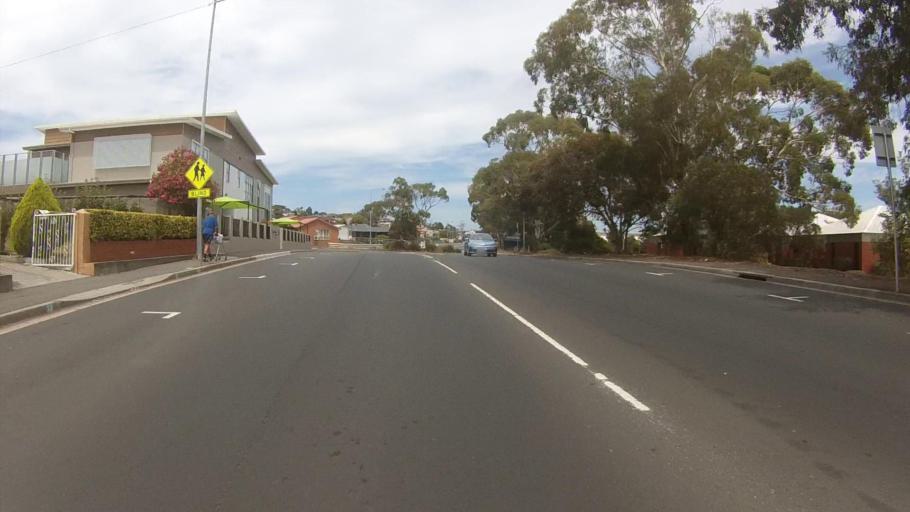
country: AU
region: Tasmania
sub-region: Clarence
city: Bellerive
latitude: -42.8626
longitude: 147.3714
